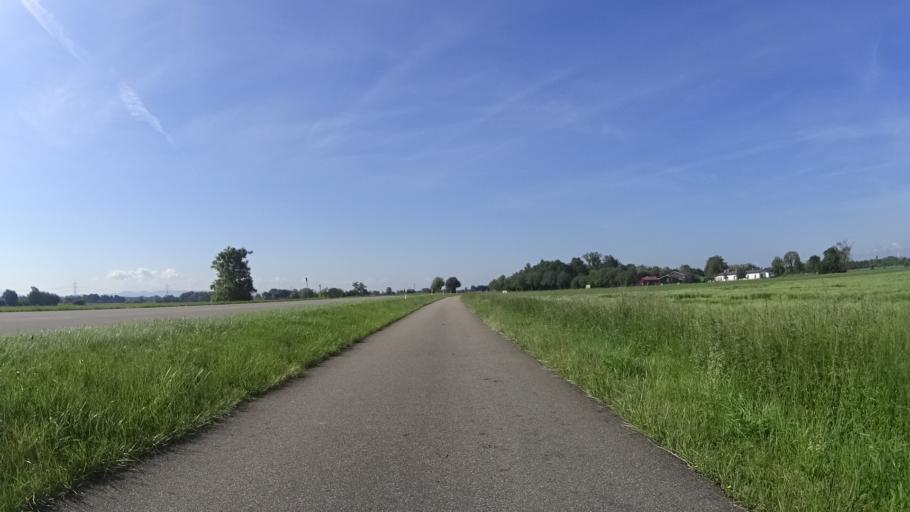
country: DE
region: Baden-Wuerttemberg
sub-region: Freiburg Region
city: Kehl
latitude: 48.5412
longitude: 7.8340
